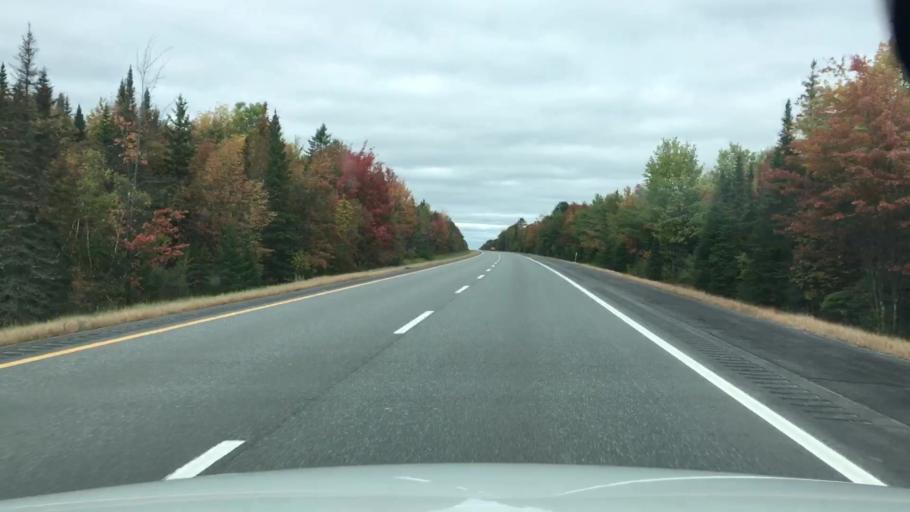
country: US
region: Maine
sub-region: Waldo County
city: Burnham
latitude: 44.7132
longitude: -69.4474
